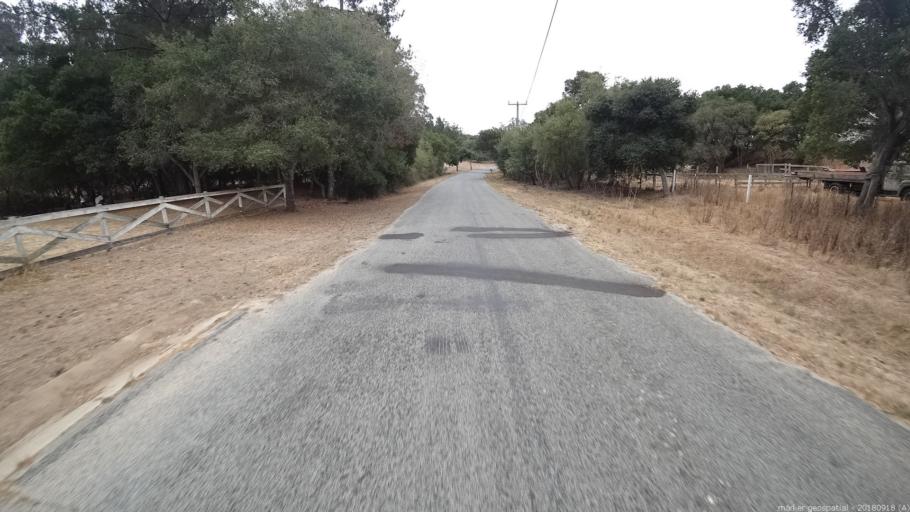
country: US
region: California
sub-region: Monterey County
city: Prunedale
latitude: 36.7847
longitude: -121.6415
